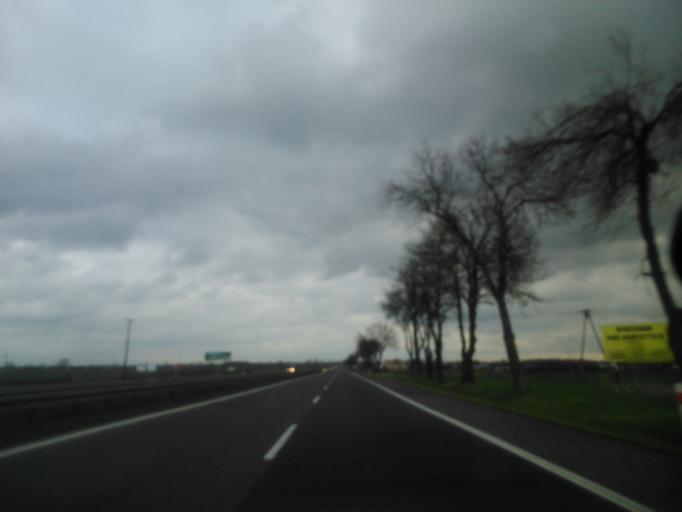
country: PL
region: Masovian Voivodeship
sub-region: Powiat plonski
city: Plonsk
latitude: 52.5981
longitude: 20.4208
